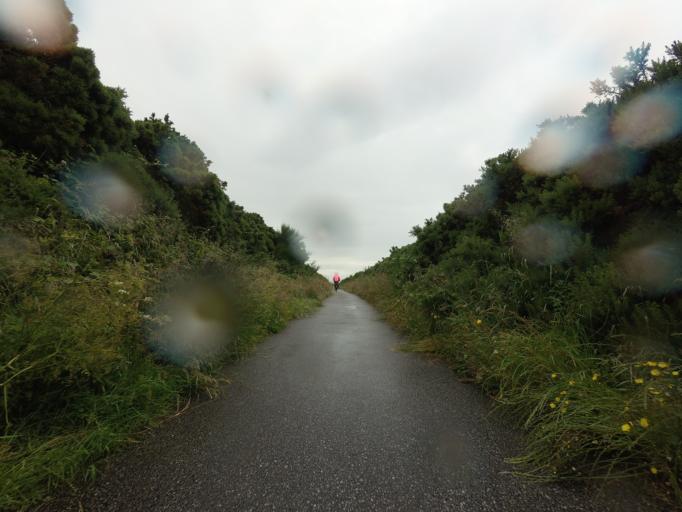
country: GB
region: Scotland
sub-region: Moray
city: Findochty
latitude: 57.6924
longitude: -2.9101
